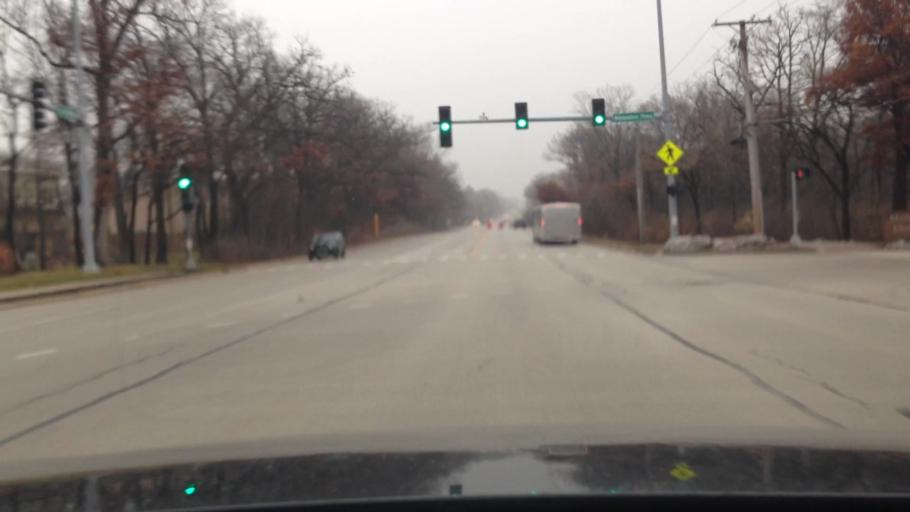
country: US
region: Illinois
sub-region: DuPage County
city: Downers Grove
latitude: 41.8313
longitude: -88.0000
